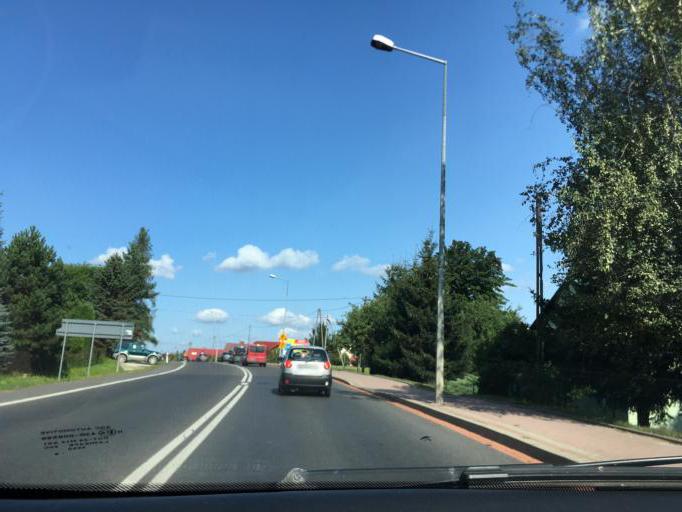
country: PL
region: Subcarpathian Voivodeship
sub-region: Powiat sanocki
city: Zagorz
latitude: 49.5157
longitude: 22.2655
